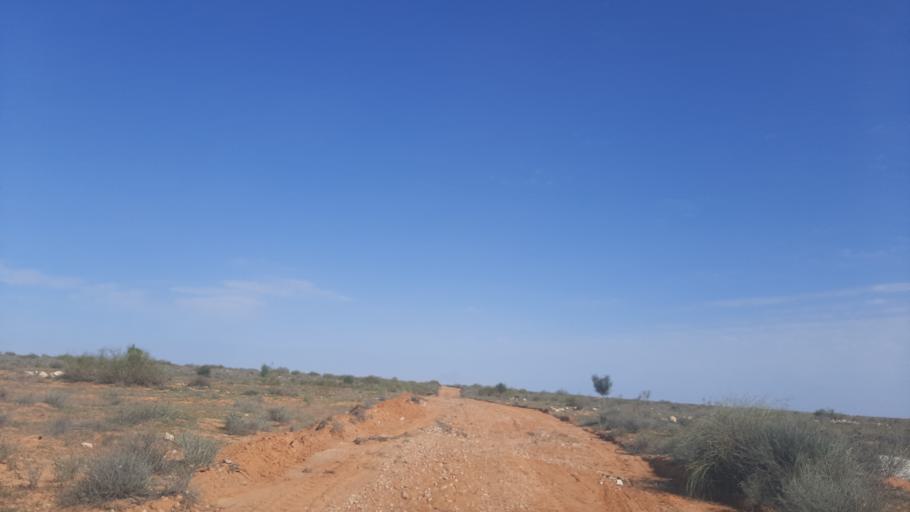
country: TN
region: Madanin
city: Medenine
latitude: 33.2435
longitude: 10.7413
